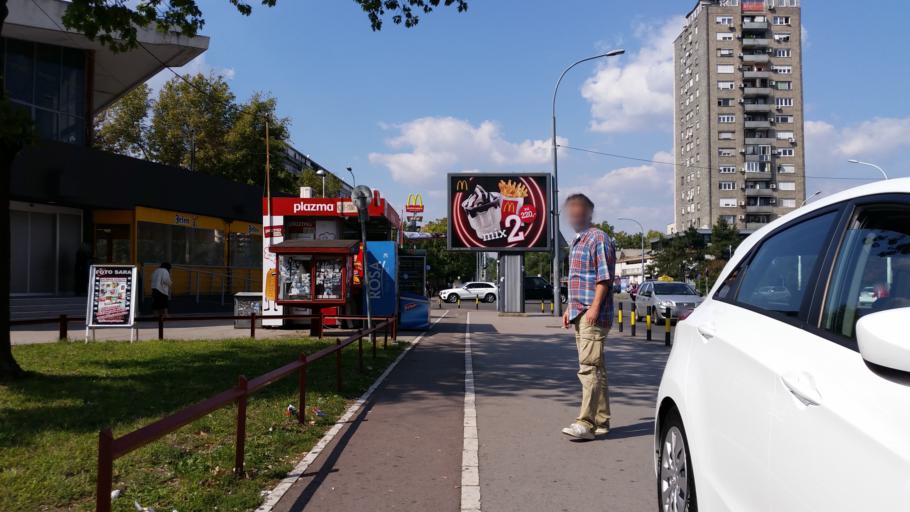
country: RS
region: Central Serbia
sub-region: Belgrade
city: Zemun
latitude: 44.8257
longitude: 20.4094
